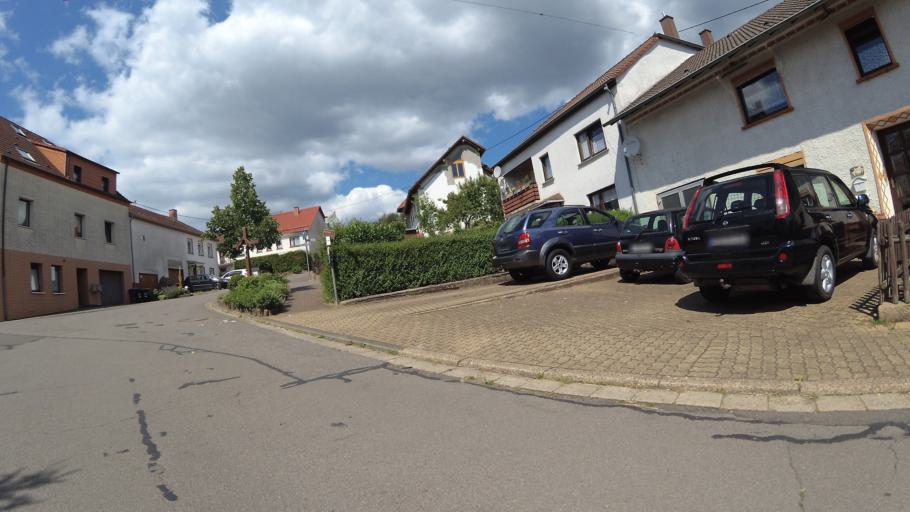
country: DE
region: Saarland
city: Weiskirchen
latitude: 49.5502
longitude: 6.7864
